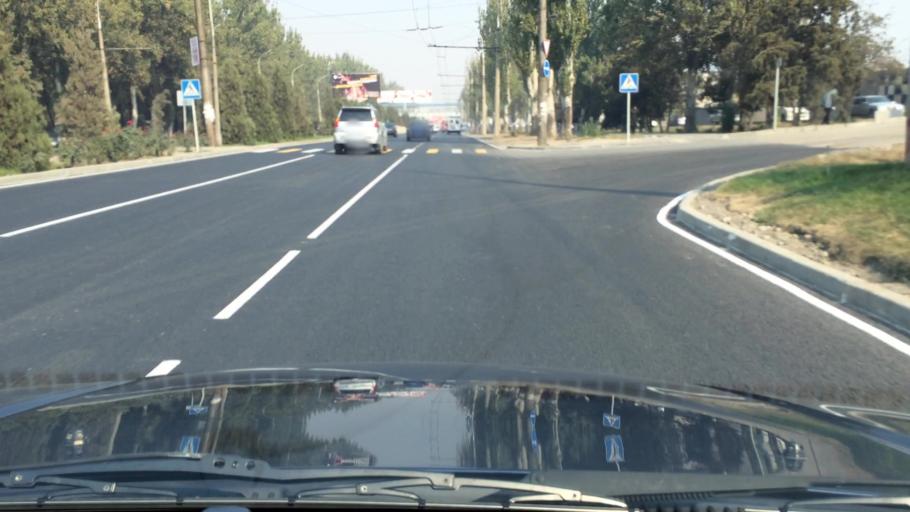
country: KG
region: Chuy
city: Lebedinovka
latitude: 42.8688
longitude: 74.6367
